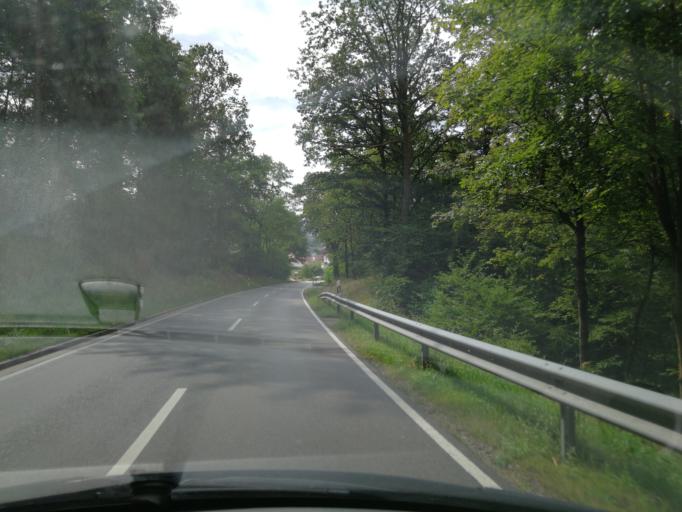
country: DE
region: Bavaria
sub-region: Upper Palatinate
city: Wiesent
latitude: 49.0186
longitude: 12.3720
